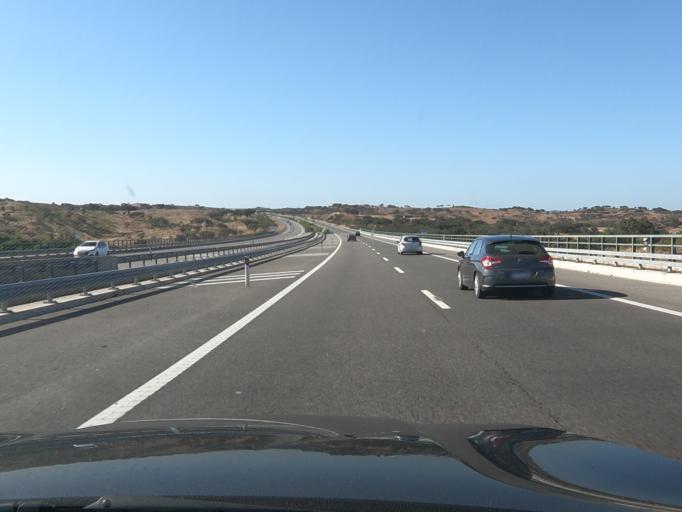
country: PT
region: Beja
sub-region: Ourique
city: Ourique
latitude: 37.5569
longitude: -8.1920
